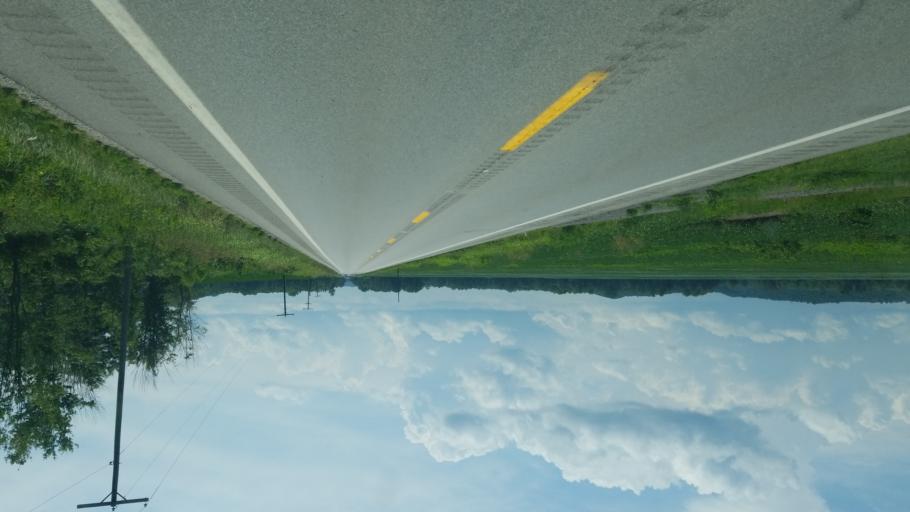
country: US
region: West Virginia
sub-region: Putnam County
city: Buffalo
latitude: 38.7000
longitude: -81.9663
